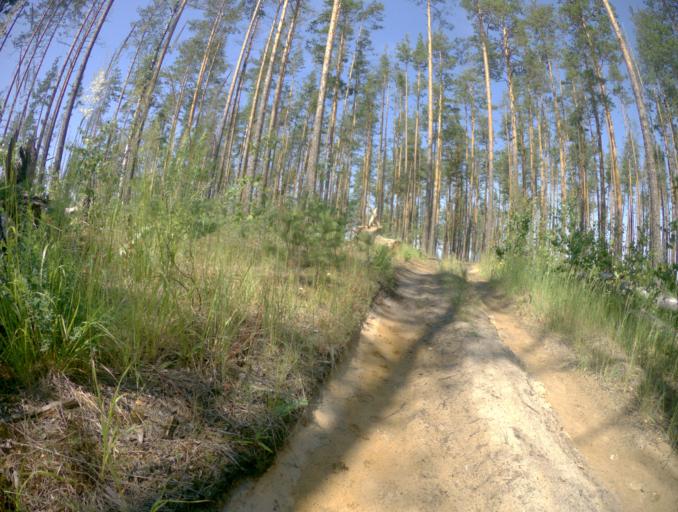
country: RU
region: Ivanovo
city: Talitsy
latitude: 56.4123
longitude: 42.2737
